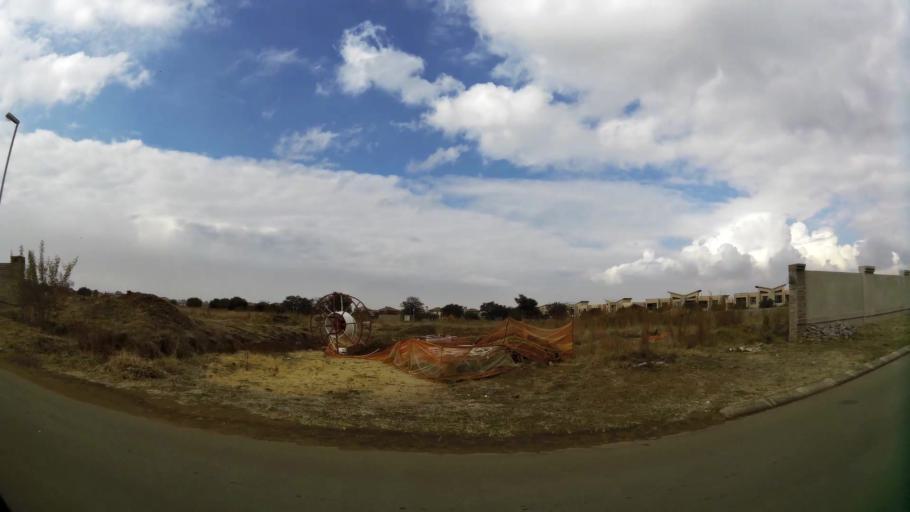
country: ZA
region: Gauteng
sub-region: Sedibeng District Municipality
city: Vanderbijlpark
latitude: -26.7244
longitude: 27.8647
